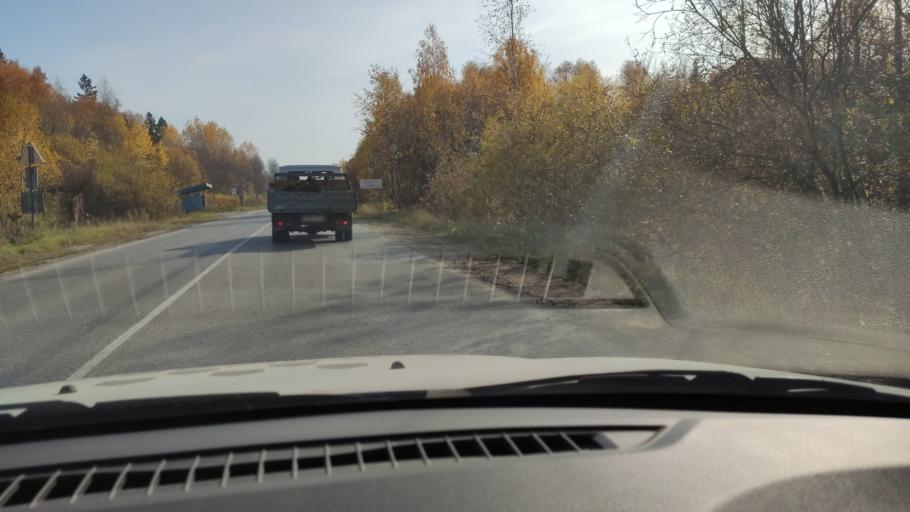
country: RU
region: Perm
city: Novyye Lyady
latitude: 58.0270
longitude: 56.6294
